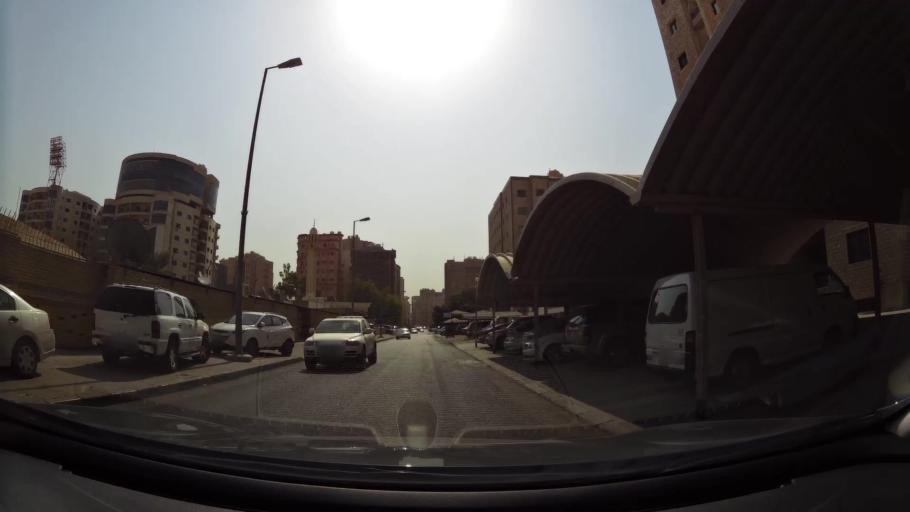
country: KW
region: Muhafazat Hawalli
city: Hawalli
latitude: 29.3395
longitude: 48.0298
